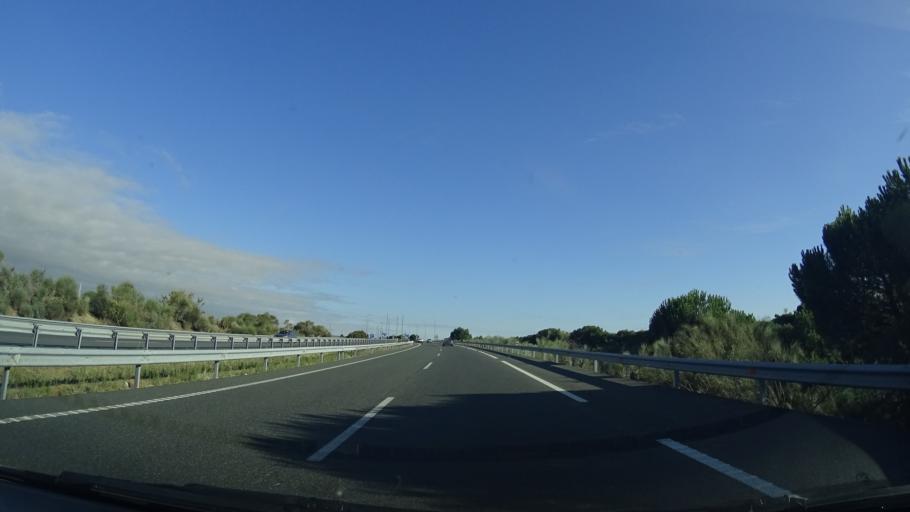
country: ES
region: Castille and Leon
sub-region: Provincia de Avila
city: Sanchidrian
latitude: 40.8771
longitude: -4.5676
